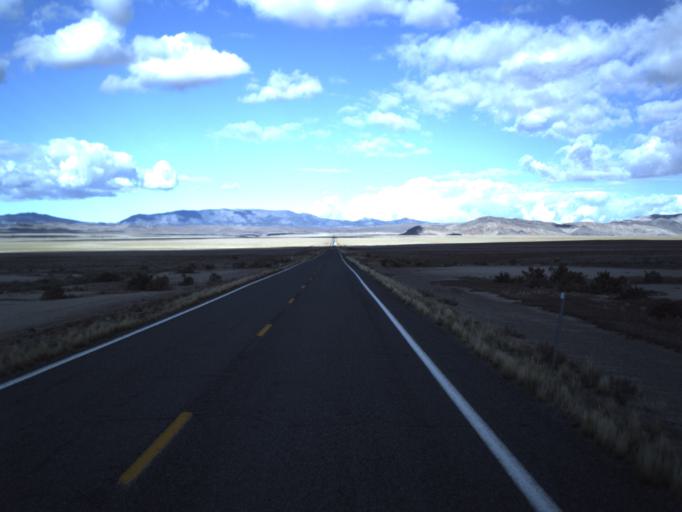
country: US
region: Utah
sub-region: Beaver County
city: Milford
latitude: 38.5490
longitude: -113.7270
